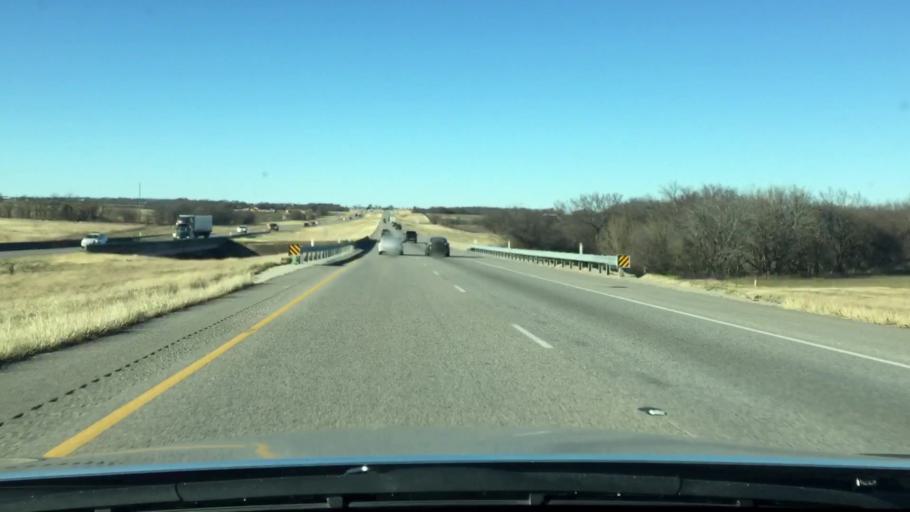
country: US
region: Texas
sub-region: Johnson County
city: Grandview
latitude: 32.2416
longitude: -97.1575
